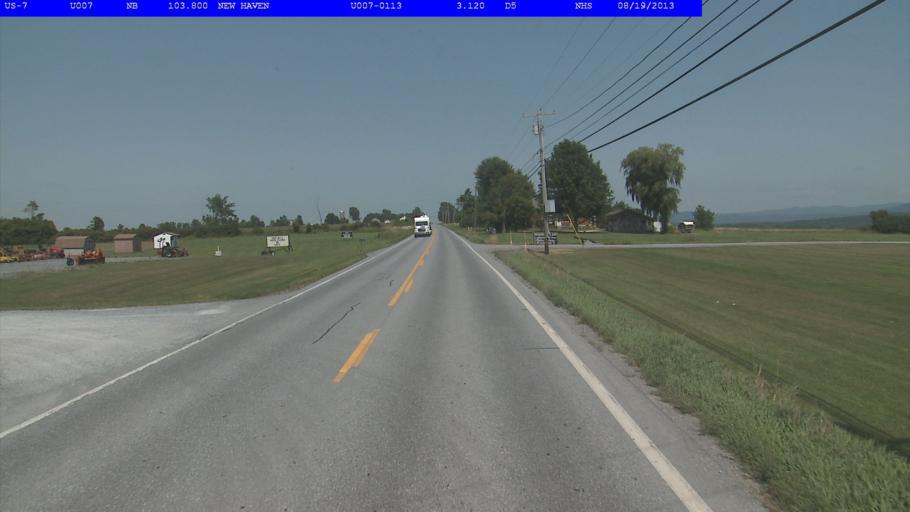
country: US
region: Vermont
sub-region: Addison County
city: Middlebury (village)
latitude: 44.0904
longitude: -73.1745
